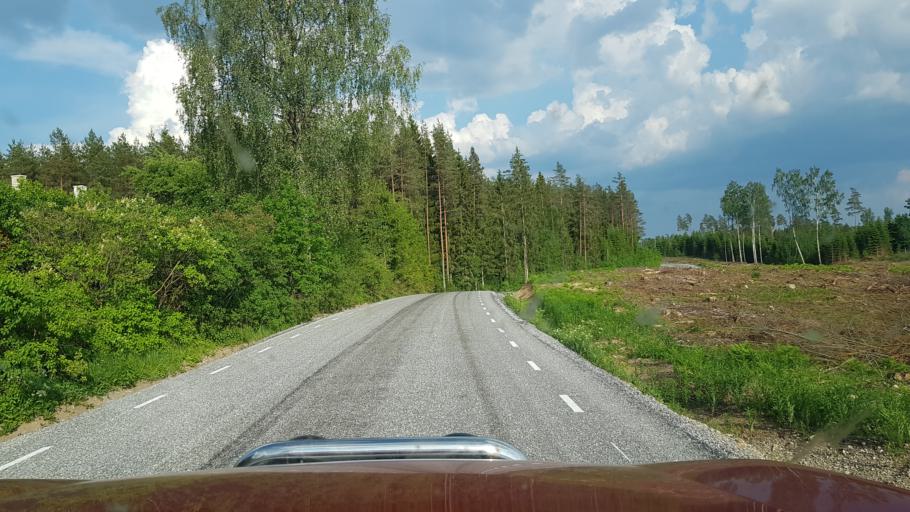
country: EE
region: Tartu
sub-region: UElenurme vald
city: Ulenurme
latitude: 58.1107
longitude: 26.7412
